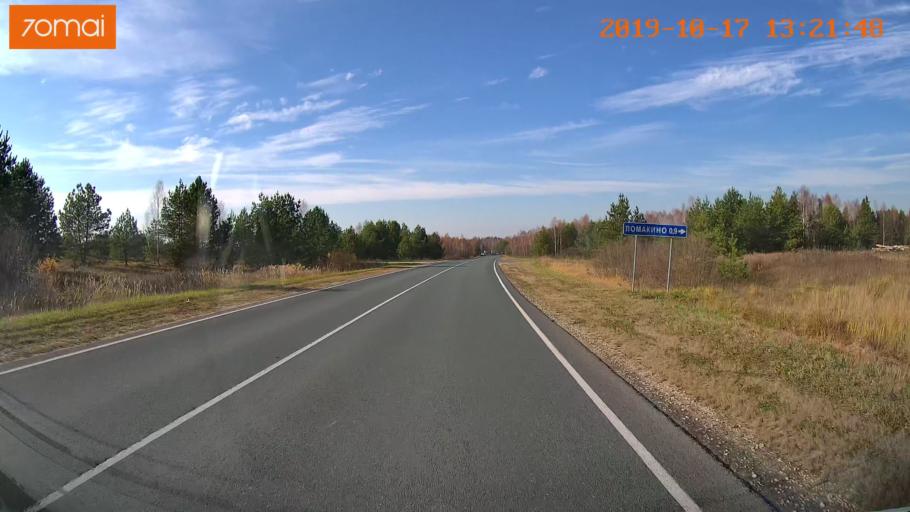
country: RU
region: Rjazan
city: Gus'-Zheleznyy
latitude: 55.0825
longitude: 41.0184
